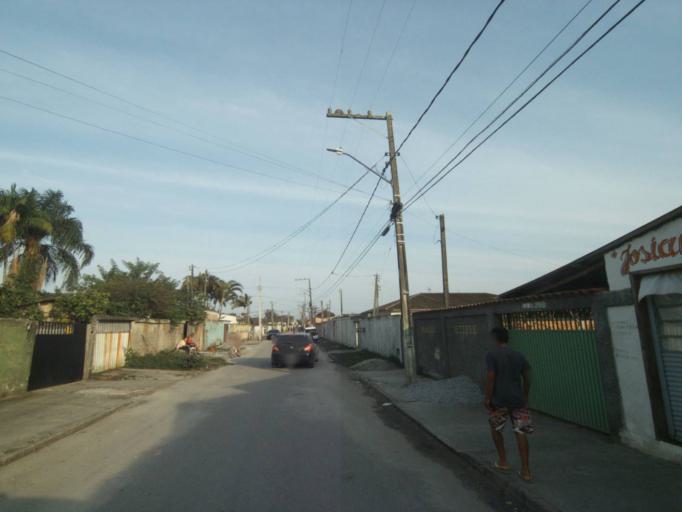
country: BR
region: Parana
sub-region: Paranagua
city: Paranagua
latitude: -25.5131
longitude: -48.5457
